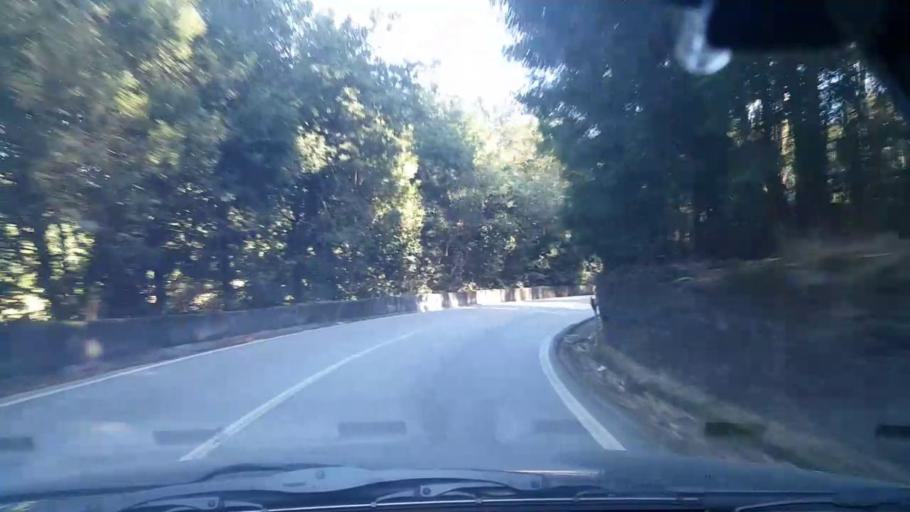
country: PT
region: Porto
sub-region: Maia
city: Gemunde
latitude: 41.3241
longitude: -8.6455
